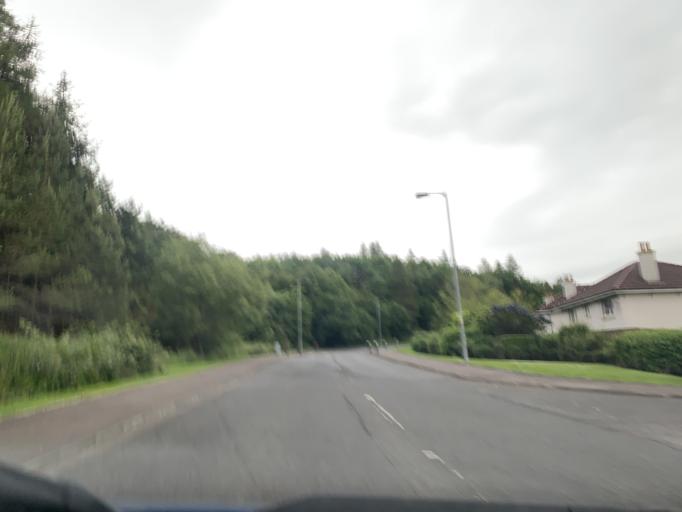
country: GB
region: Scotland
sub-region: East Renfrewshire
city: Newton Mearns
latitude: 55.7720
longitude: -4.3485
